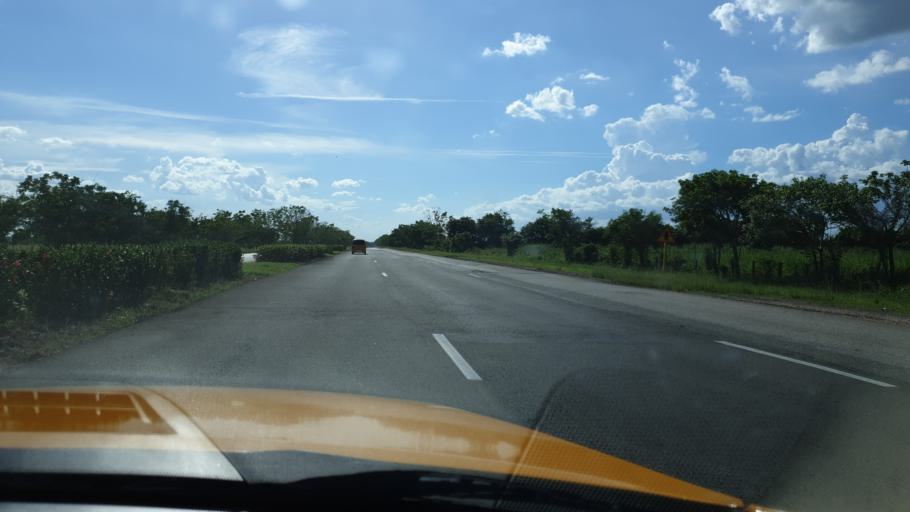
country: CU
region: Cienfuegos
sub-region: Municipio de Aguada de Pasajeros
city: Aguada de Pasajeros
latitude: 22.4106
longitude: -80.8928
